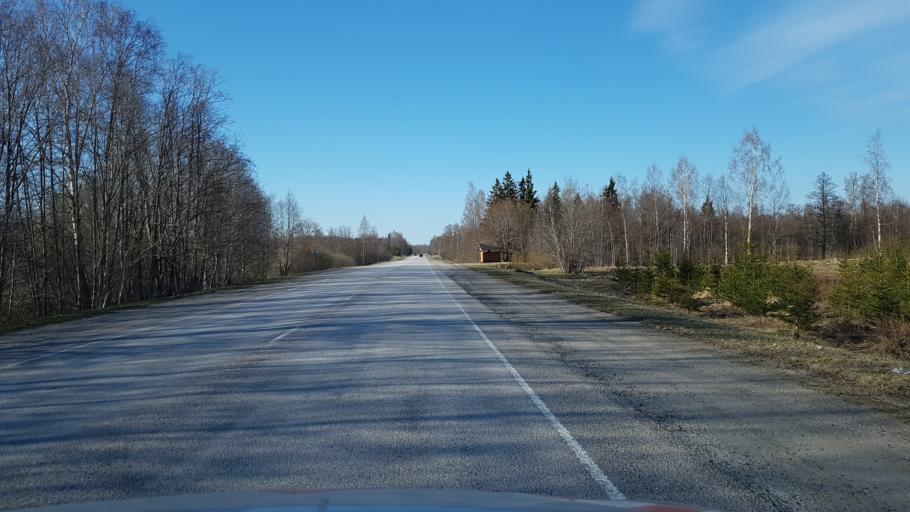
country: EE
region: Ida-Virumaa
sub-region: Johvi vald
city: Johvi
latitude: 59.1733
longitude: 27.3505
